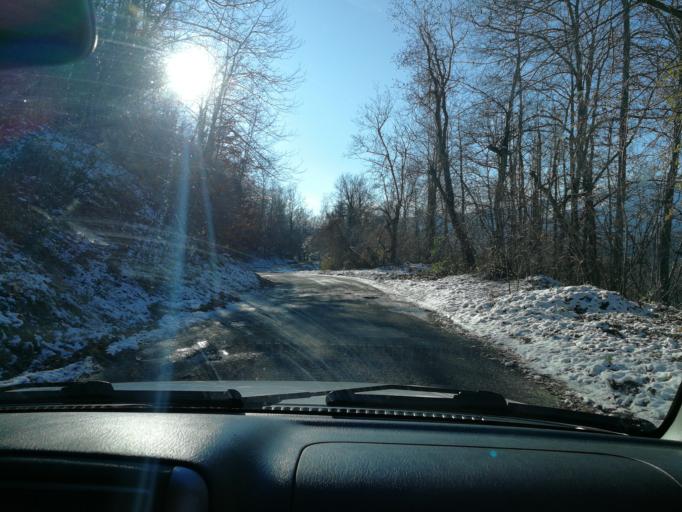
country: IT
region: Latium
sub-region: Provincia di Rieti
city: Amatrice
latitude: 42.6683
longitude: 13.2911
